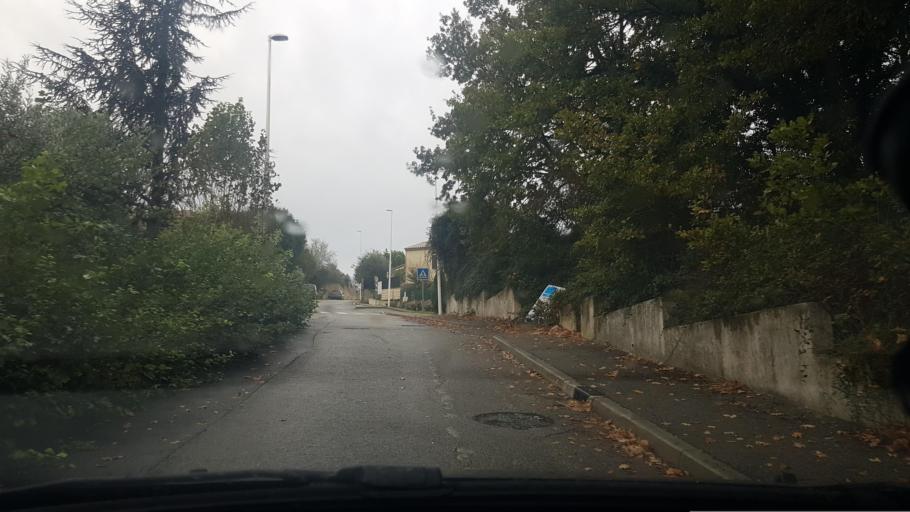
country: FR
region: Languedoc-Roussillon
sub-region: Departement du Gard
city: Bellegarde
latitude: 43.7548
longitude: 4.5049
